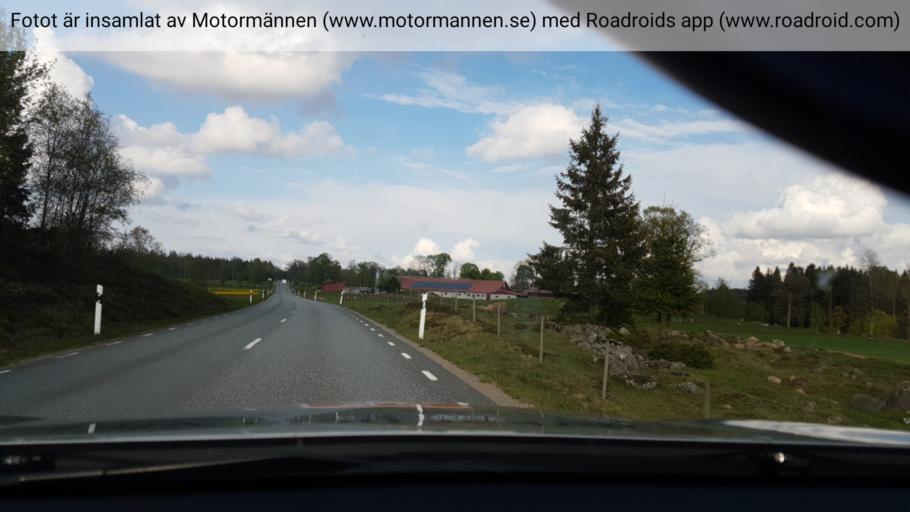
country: SE
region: Joenkoeping
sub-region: Vaggeryds Kommun
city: Skillingaryd
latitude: 57.3998
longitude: 14.0475
